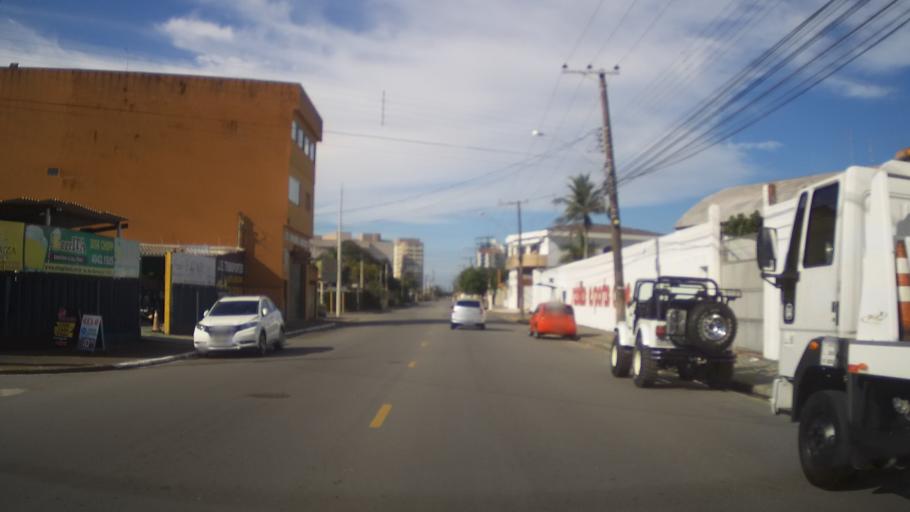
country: BR
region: Sao Paulo
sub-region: Itanhaem
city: Itanhaem
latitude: -24.1766
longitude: -46.7749
